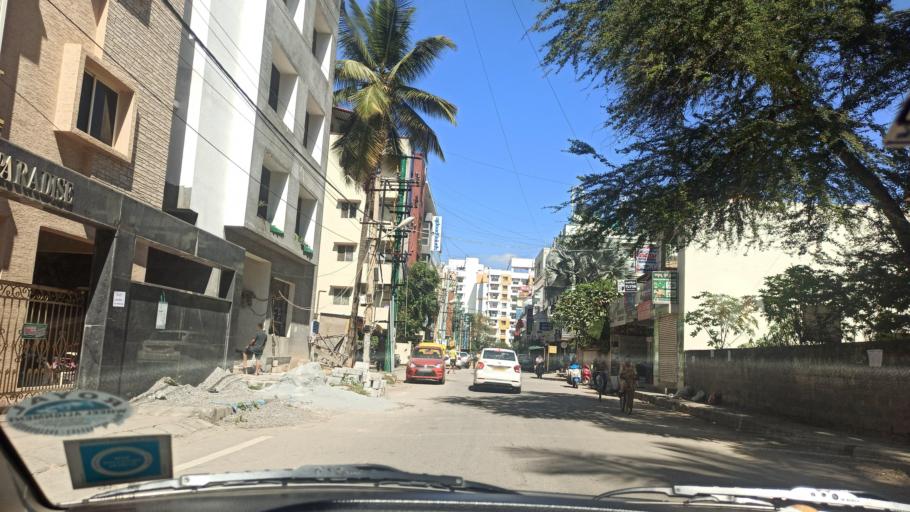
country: IN
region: Karnataka
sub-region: Bangalore Urban
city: Bangalore
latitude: 12.9256
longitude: 77.6696
